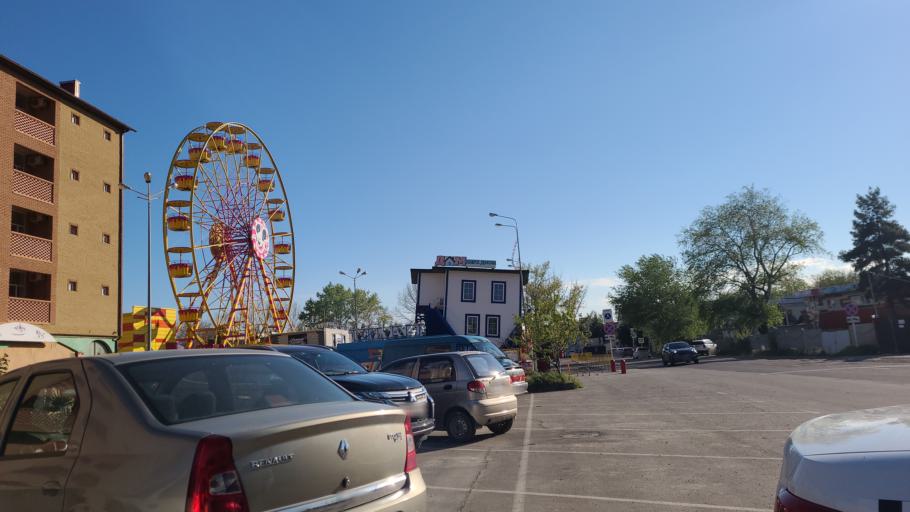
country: RU
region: Krasnodarskiy
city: Tsibanobalka
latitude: 44.9461
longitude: 37.3054
